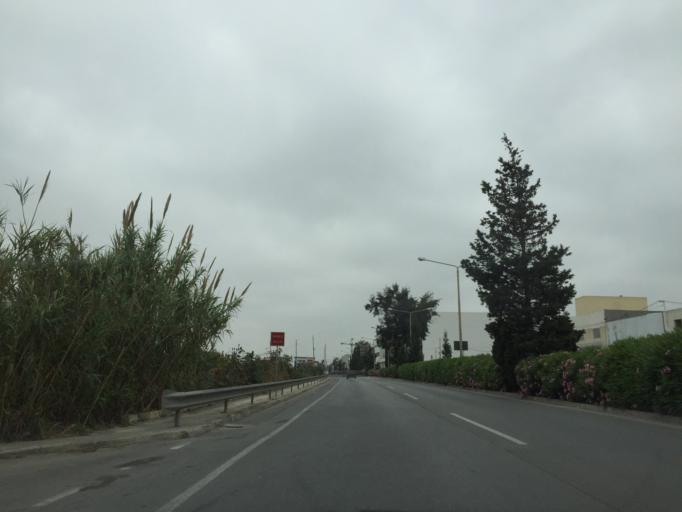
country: MT
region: Saint Venera
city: Santa Venera
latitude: 35.8872
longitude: 14.4660
